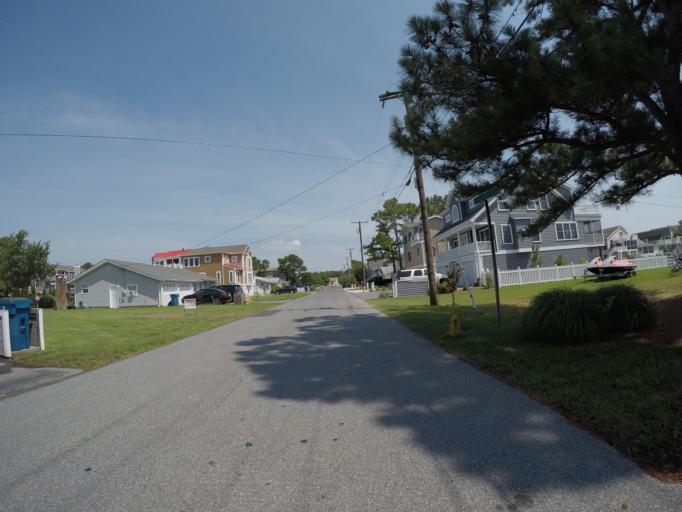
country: US
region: Delaware
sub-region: Sussex County
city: Bethany Beach
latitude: 38.5166
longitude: -75.0617
